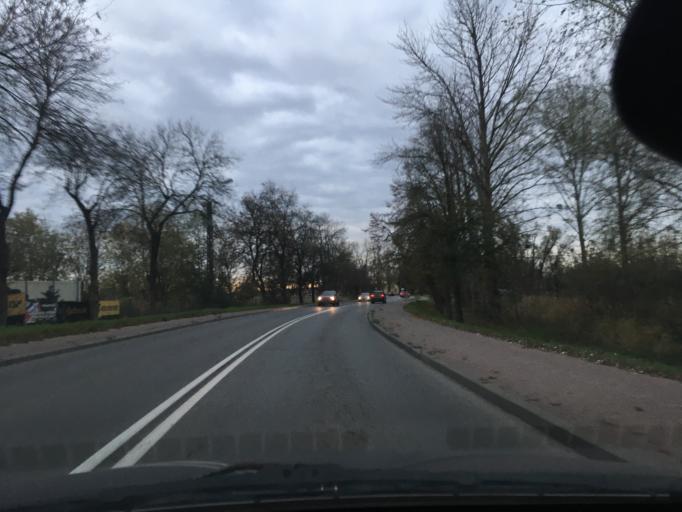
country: PL
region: Masovian Voivodeship
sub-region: Powiat piaseczynski
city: Lesznowola
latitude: 52.0903
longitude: 20.9350
